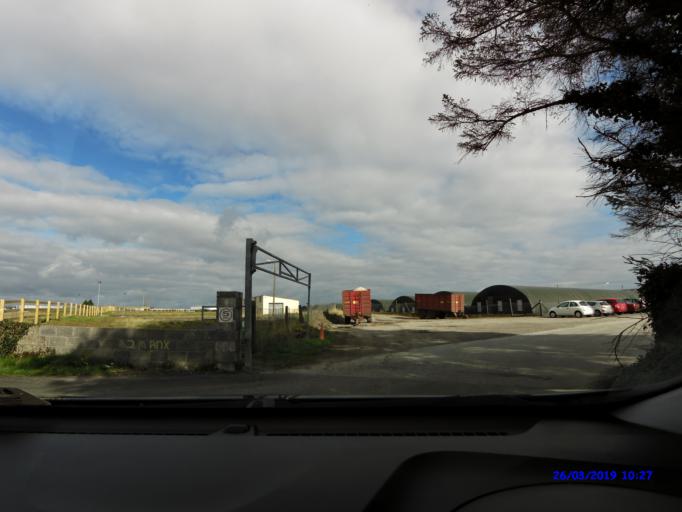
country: IE
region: Connaught
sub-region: Maigh Eo
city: Claremorris
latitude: 53.7369
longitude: -9.0025
